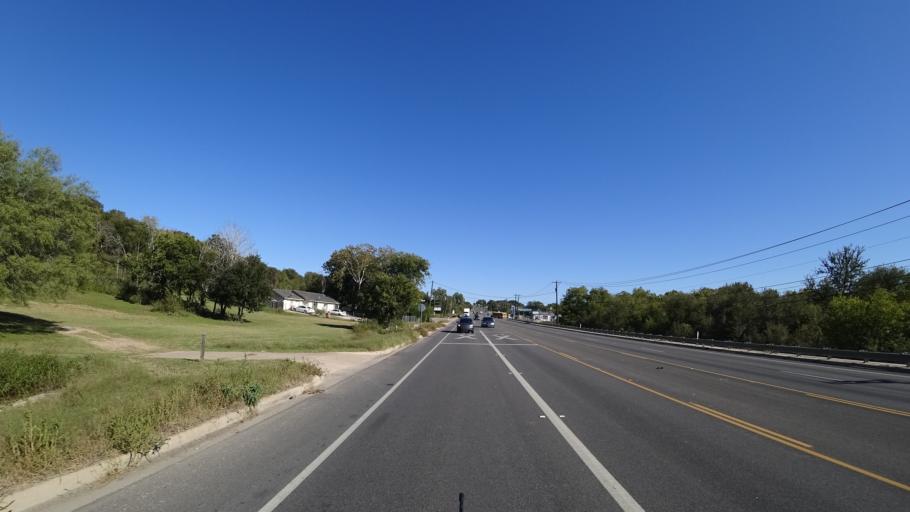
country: US
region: Texas
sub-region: Travis County
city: Hornsby Bend
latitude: 30.2806
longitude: -97.6471
